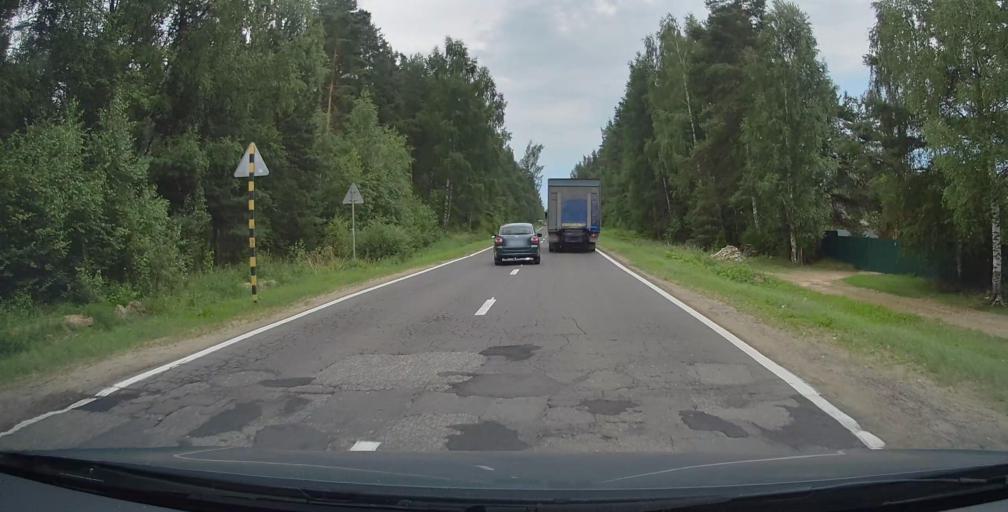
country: RU
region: Jaroslavl
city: Myshkin
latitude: 57.8532
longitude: 38.5107
